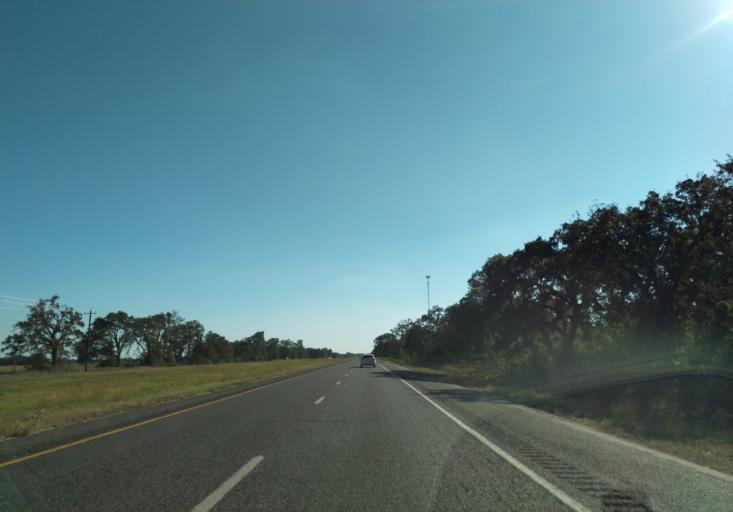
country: US
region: Texas
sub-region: Waller County
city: Hempstead
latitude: 30.1365
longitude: -96.0722
